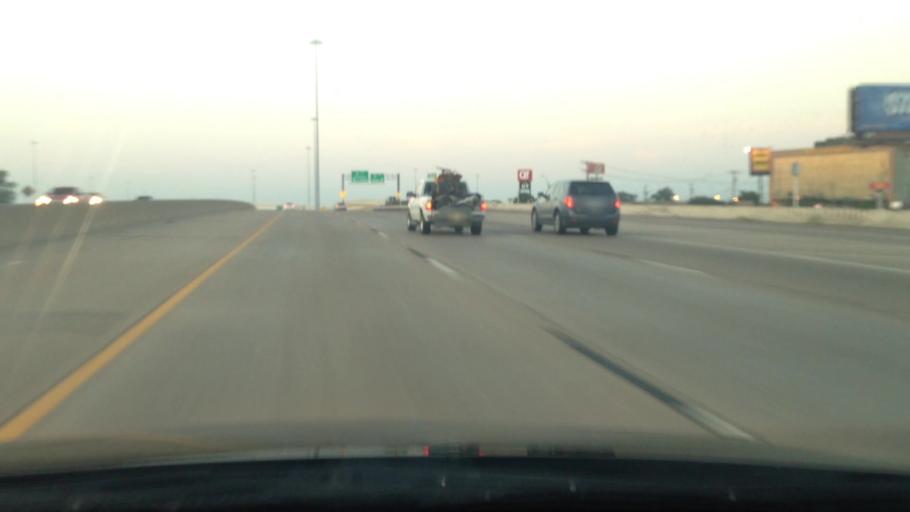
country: US
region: Texas
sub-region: Tarrant County
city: Richland Hills
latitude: 32.7531
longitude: -97.2174
